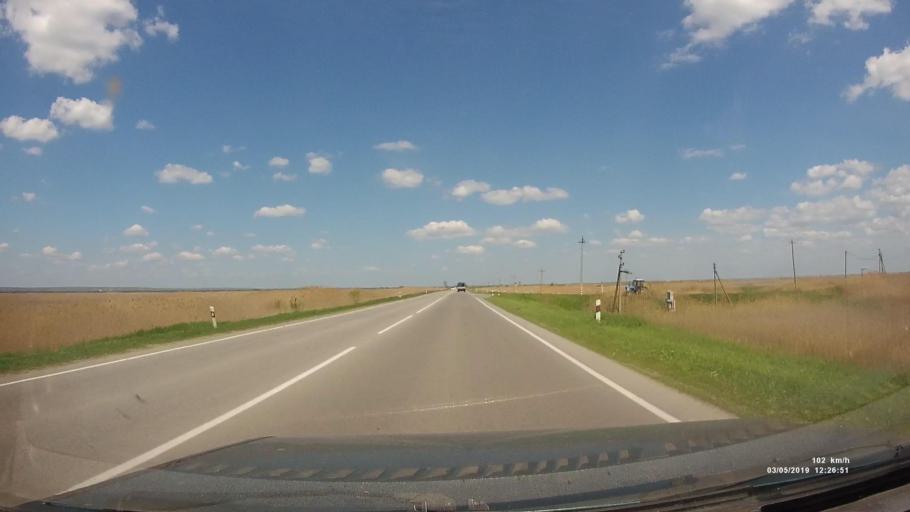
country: RU
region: Rostov
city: Semikarakorsk
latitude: 47.4514
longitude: 40.7169
